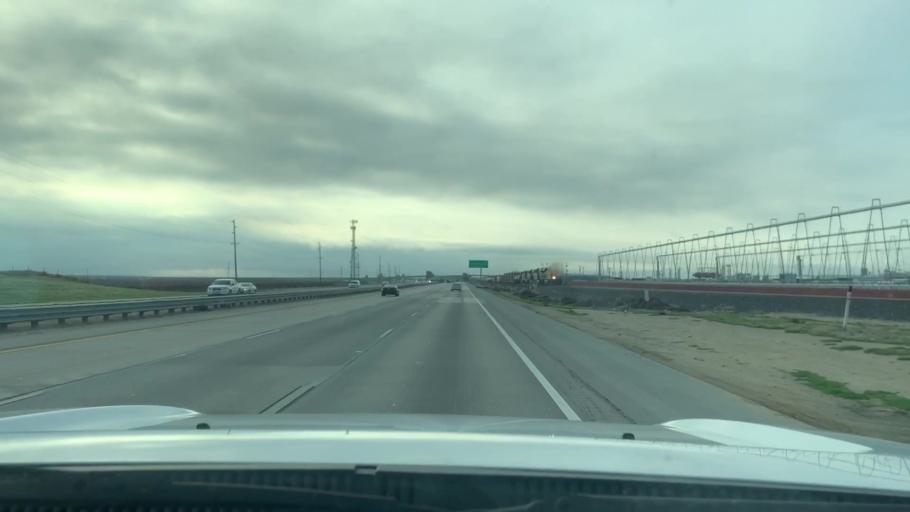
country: US
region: California
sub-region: Kern County
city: Shafter
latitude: 35.5703
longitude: -119.2011
